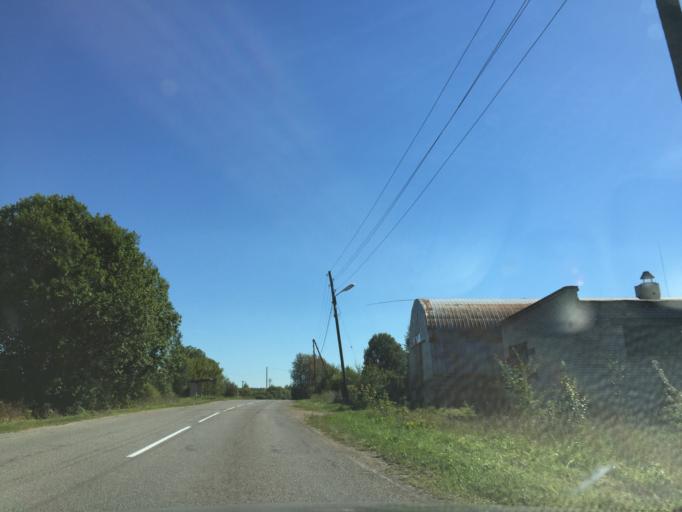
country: LV
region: Akniste
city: Akniste
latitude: 56.0527
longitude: 25.9055
